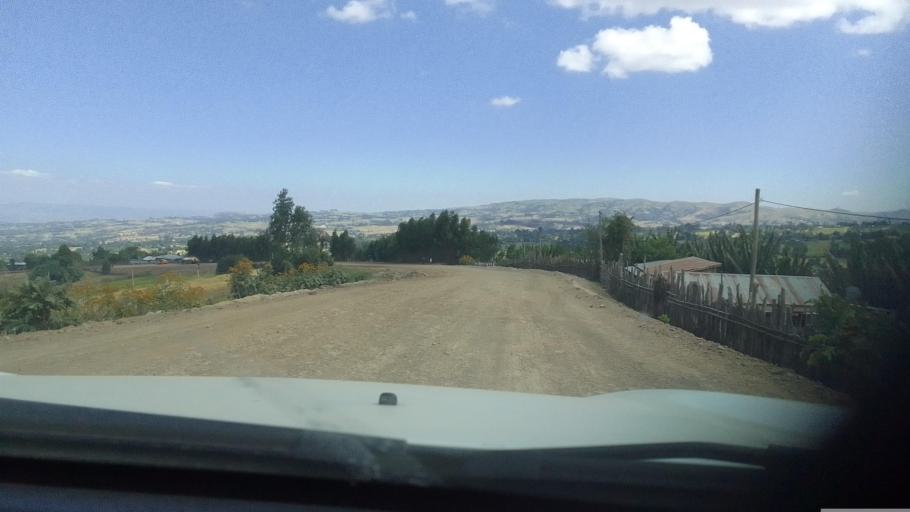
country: ET
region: Oromiya
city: Hagere Hiywet
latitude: 8.8499
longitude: 37.8906
